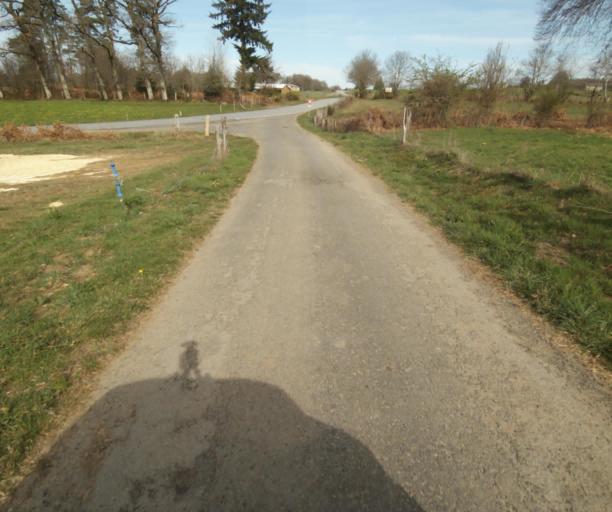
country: FR
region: Limousin
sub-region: Departement de la Correze
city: Correze
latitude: 45.3975
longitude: 1.8279
